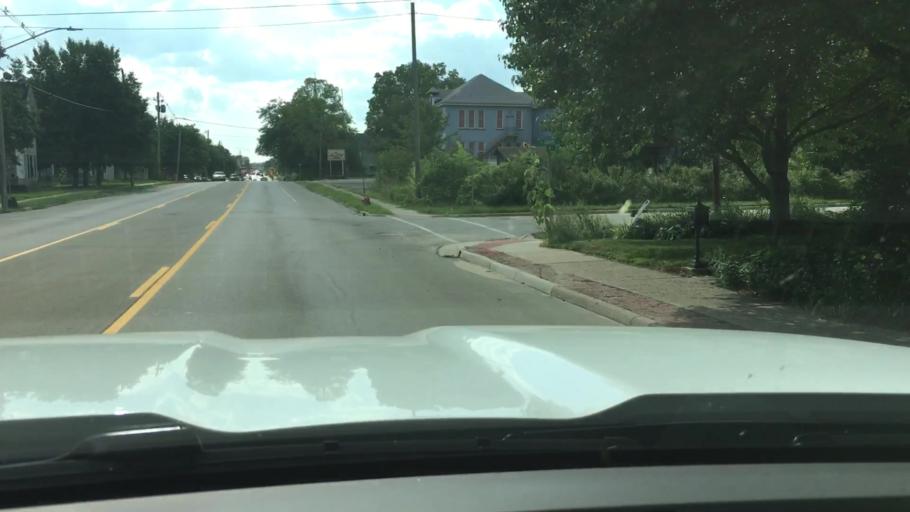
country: US
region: Michigan
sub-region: Kent County
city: Lowell
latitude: 42.9363
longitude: -85.3290
